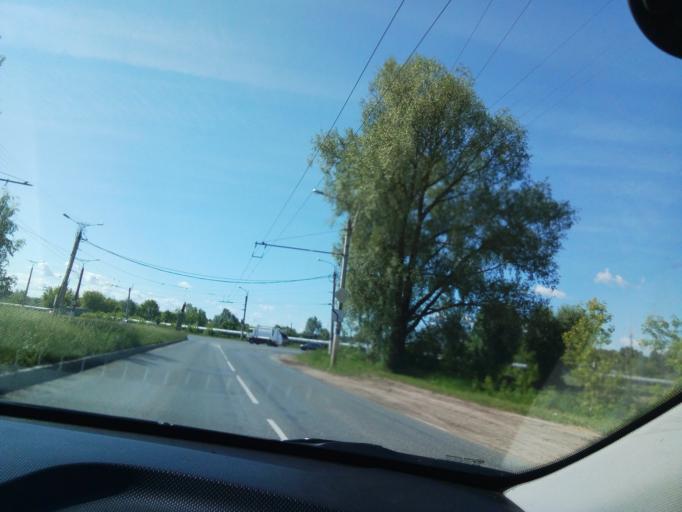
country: RU
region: Chuvashia
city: Novocheboksarsk
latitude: 56.0954
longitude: 47.4944
